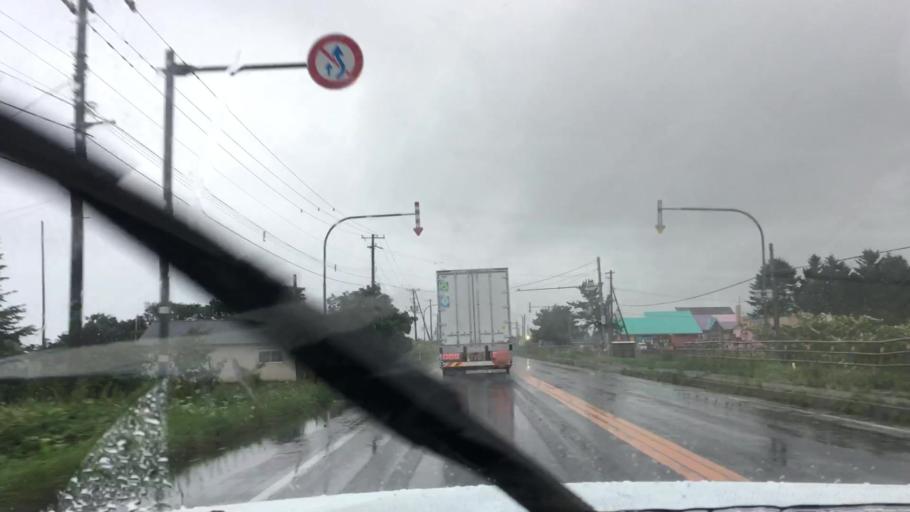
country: JP
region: Hokkaido
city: Niseko Town
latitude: 42.4759
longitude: 140.3471
